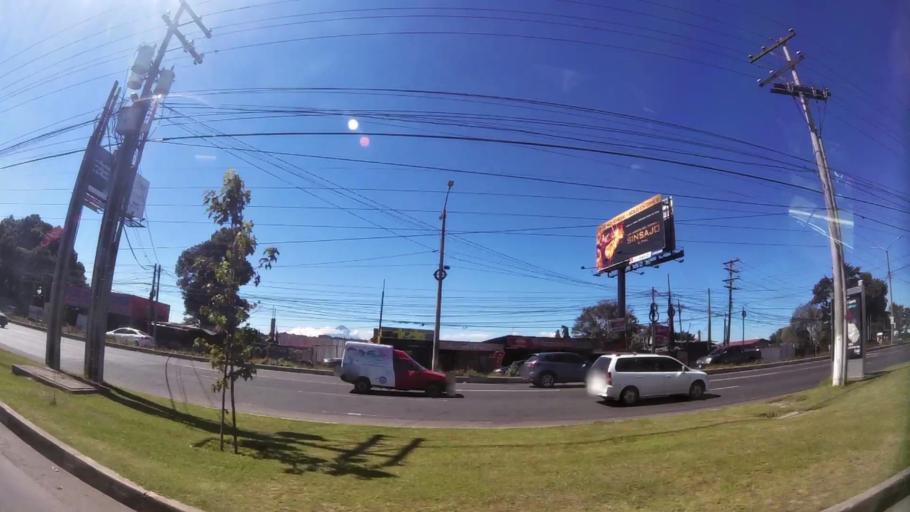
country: GT
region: Guatemala
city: San Jose Pinula
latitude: 14.5507
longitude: -90.4548
